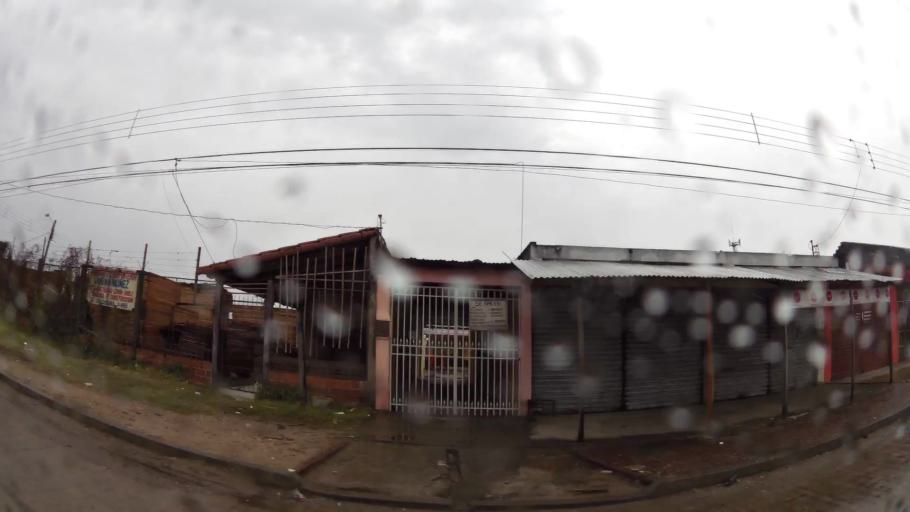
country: BO
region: Santa Cruz
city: Santa Cruz de la Sierra
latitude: -17.8043
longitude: -63.1356
